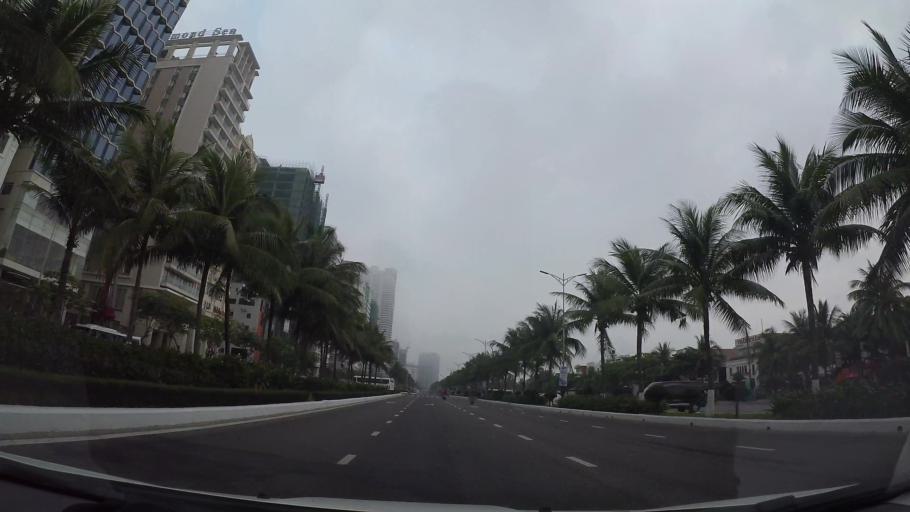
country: VN
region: Da Nang
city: Son Tra
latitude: 16.0660
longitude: 108.2454
